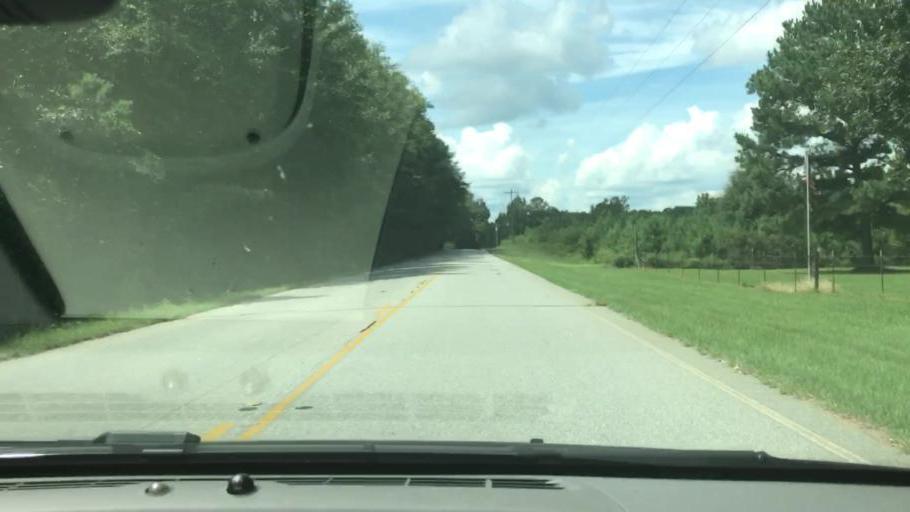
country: US
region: Georgia
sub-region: Stewart County
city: Lumpkin
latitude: 32.1377
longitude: -84.9521
